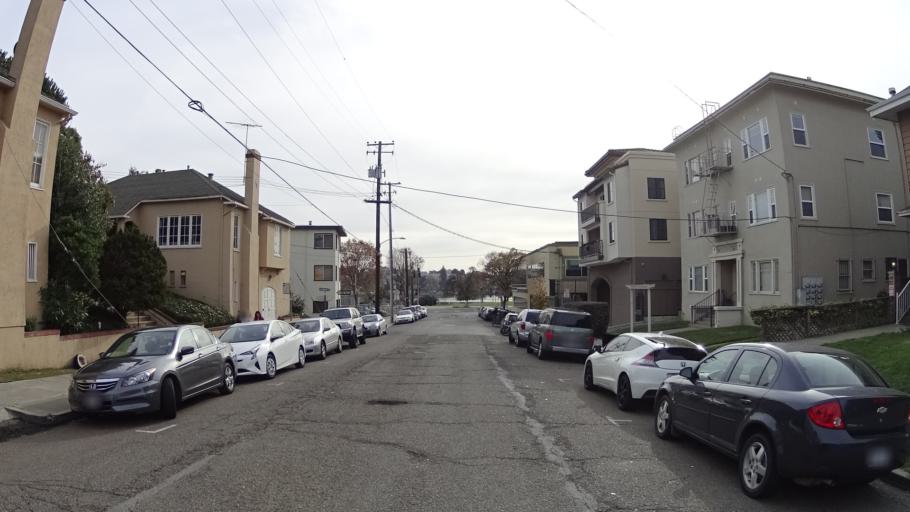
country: US
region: California
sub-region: Alameda County
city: Oakland
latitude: 37.8095
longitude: -122.2516
